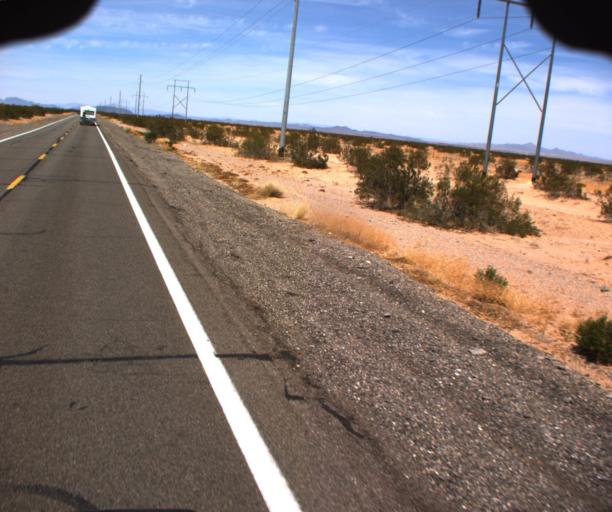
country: US
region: Arizona
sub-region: La Paz County
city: Parker
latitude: 33.9326
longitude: -114.2169
